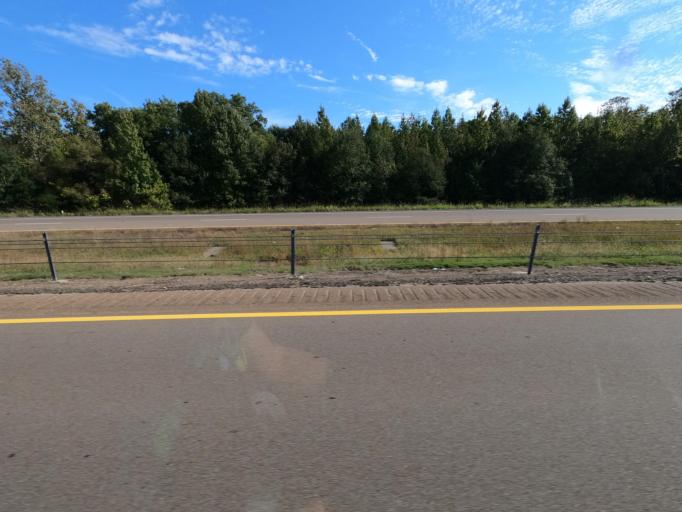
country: US
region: Tennessee
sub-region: Shelby County
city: Arlington
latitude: 35.2838
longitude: -89.6819
